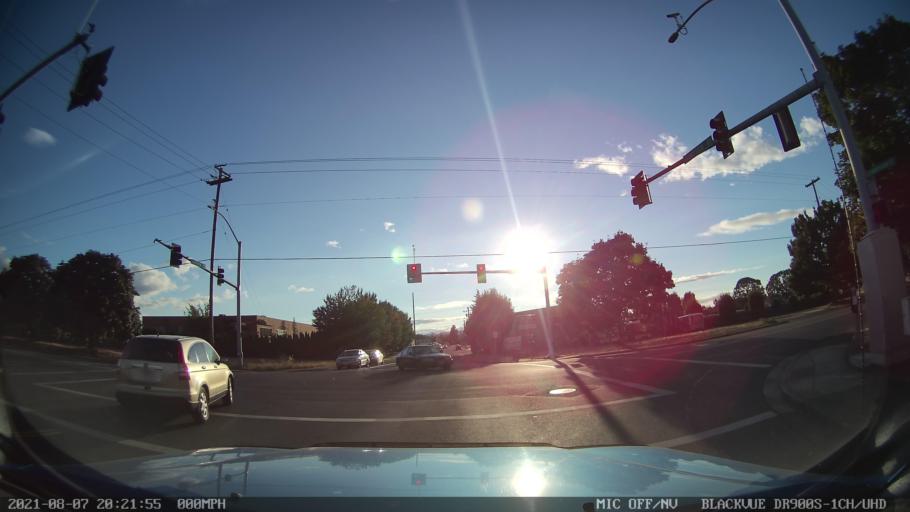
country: US
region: Oregon
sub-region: Marion County
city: Salem
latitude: 44.9563
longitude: -123.0105
